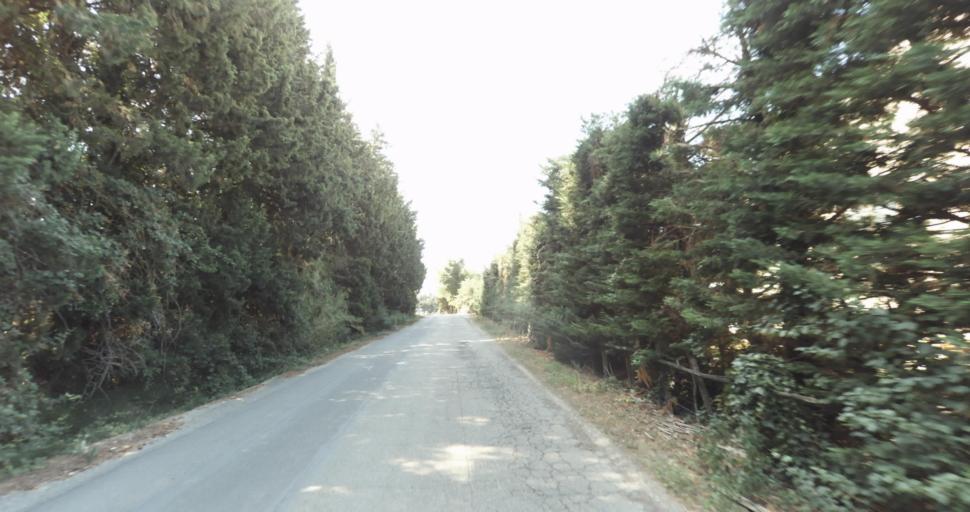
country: FR
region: Provence-Alpes-Cote d'Azur
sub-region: Departement du Vaucluse
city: Carpentras
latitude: 44.0313
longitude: 5.0276
